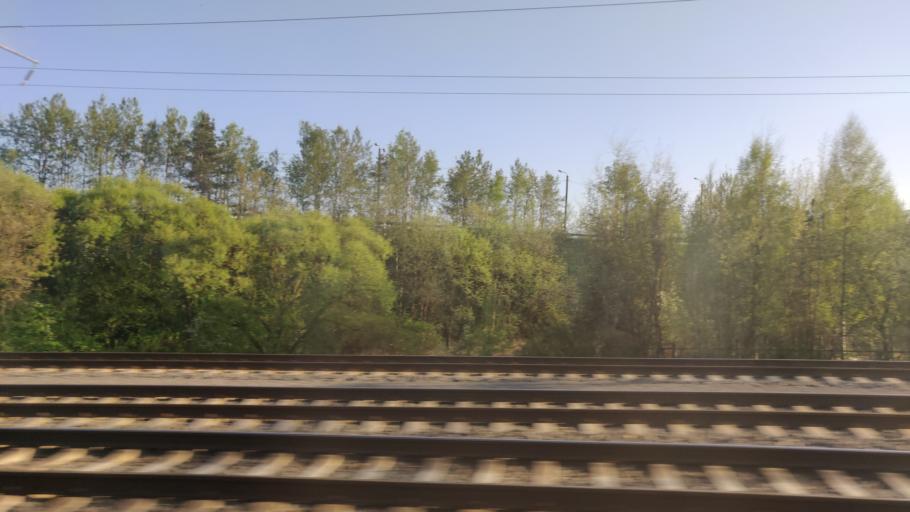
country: LT
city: Baltoji Voke
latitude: 54.6316
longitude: 25.1428
